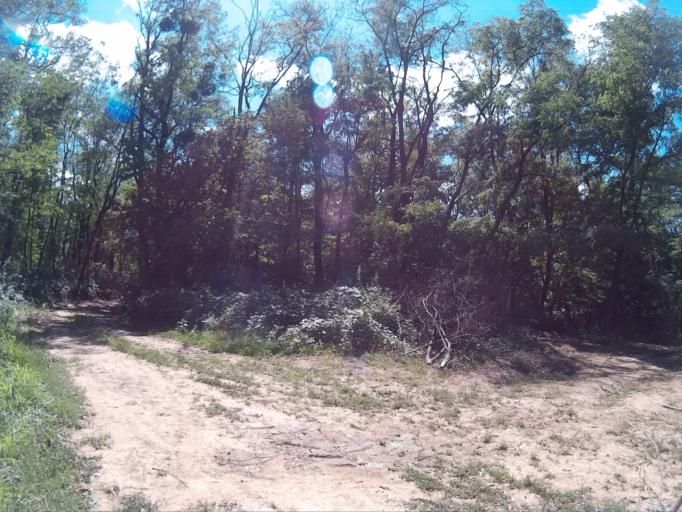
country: HU
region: Zala
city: Zalalovo
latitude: 46.8143
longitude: 16.6018
